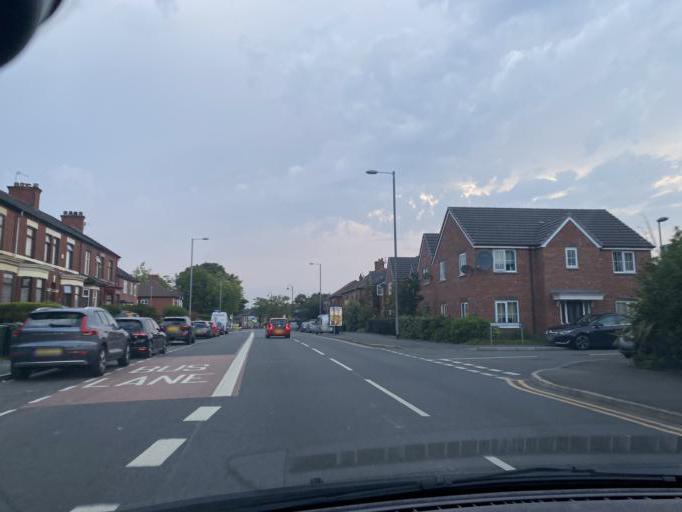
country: GB
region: England
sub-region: Borough of Tameside
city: Droylsden
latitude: 53.4739
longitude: -2.1396
